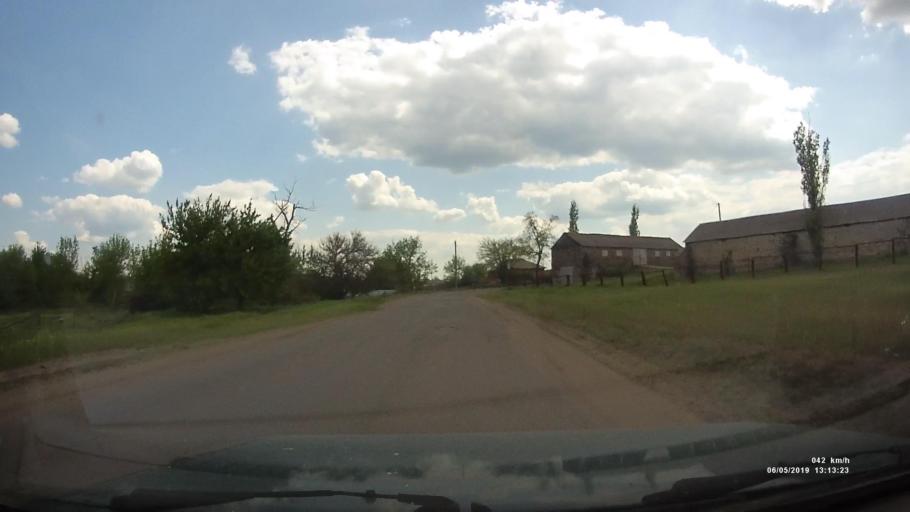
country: RU
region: Rostov
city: Ust'-Donetskiy
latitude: 47.7534
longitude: 40.9392
